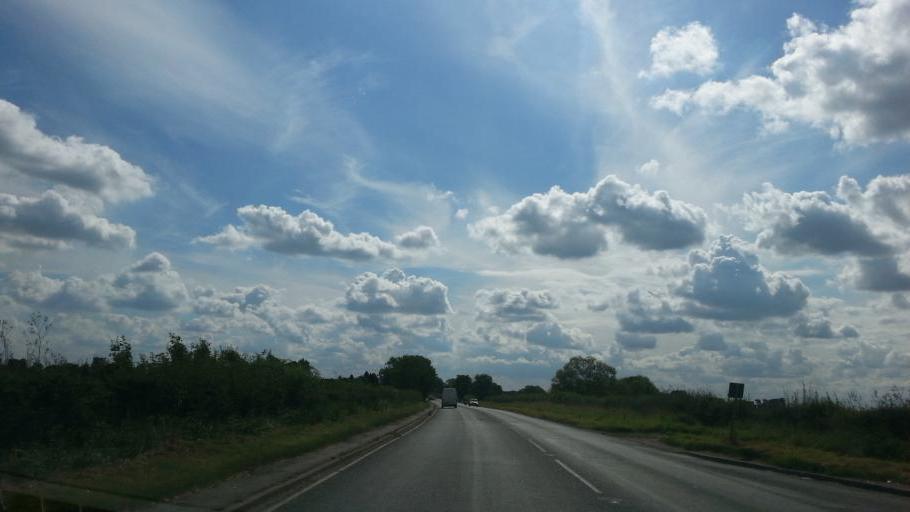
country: GB
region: England
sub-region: Nottinghamshire
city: Newark on Trent
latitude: 53.1128
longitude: -0.8204
